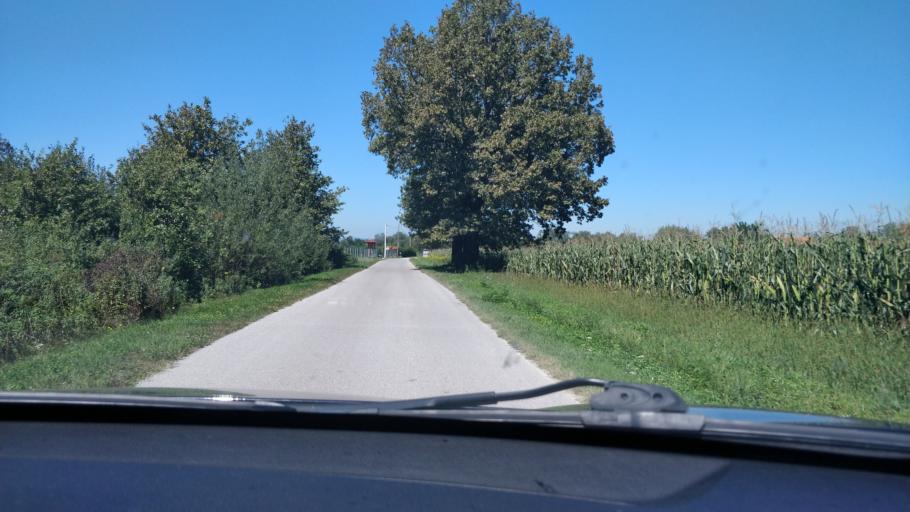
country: HR
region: Karlovacka
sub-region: Grad Karlovac
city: Karlovac
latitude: 45.4739
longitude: 15.6606
